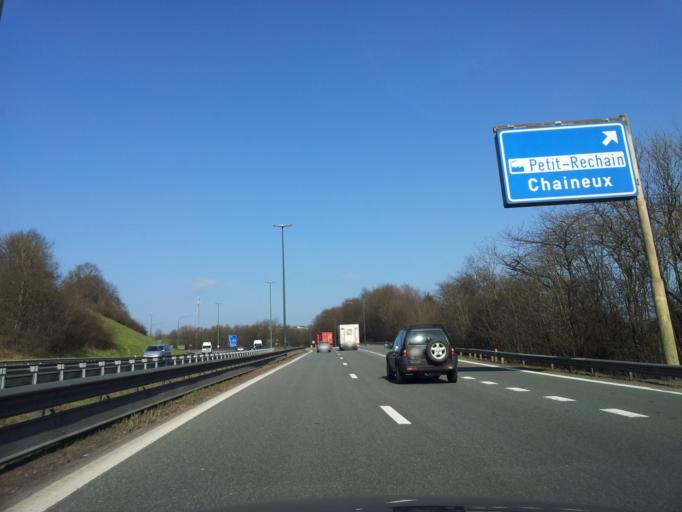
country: BE
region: Wallonia
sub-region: Province de Liege
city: Dison
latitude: 50.6260
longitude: 5.8508
